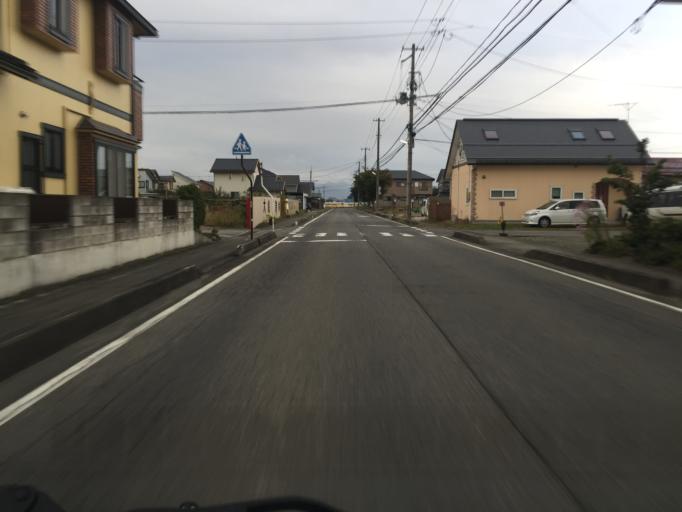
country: JP
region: Fukushima
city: Kitakata
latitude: 37.5123
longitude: 139.8773
